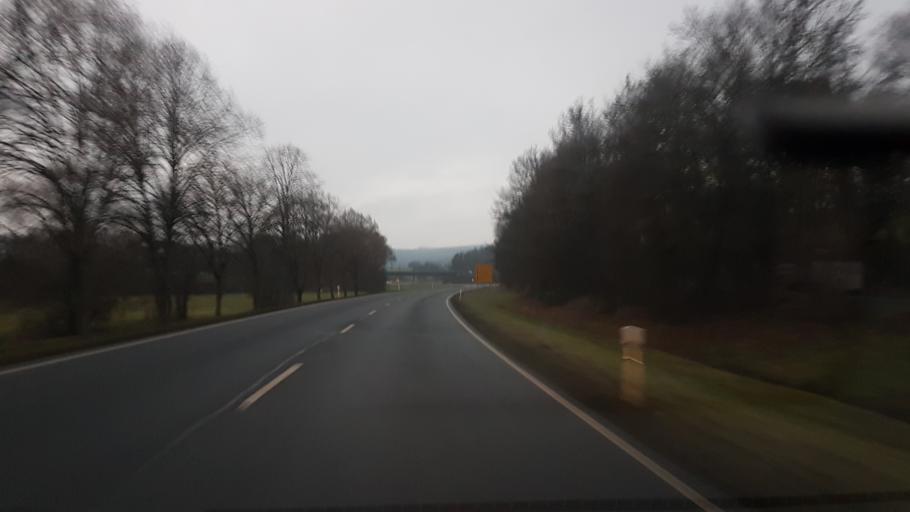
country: DE
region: Bavaria
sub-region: Regierungsbezirk Unterfranken
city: Pfarrweisach
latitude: 50.1726
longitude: 10.7135
